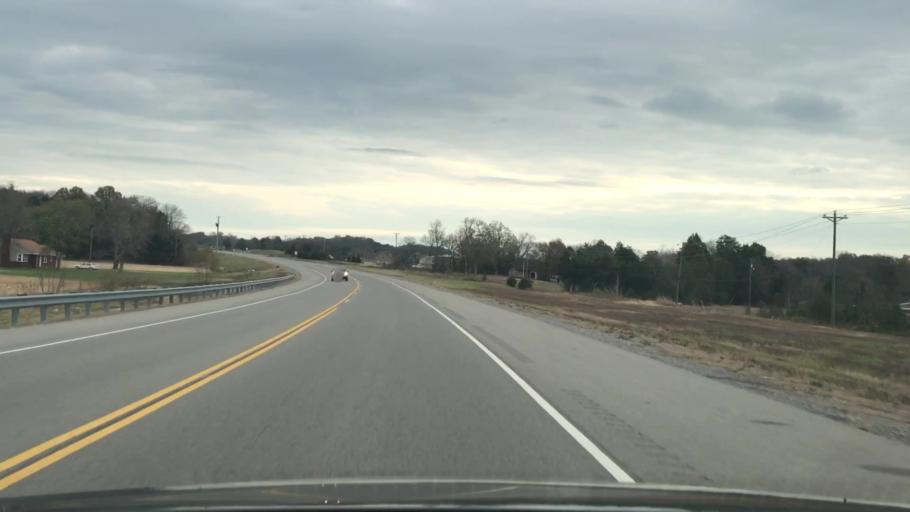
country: US
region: Tennessee
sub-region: Trousdale County
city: Hartsville
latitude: 36.2896
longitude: -86.2064
